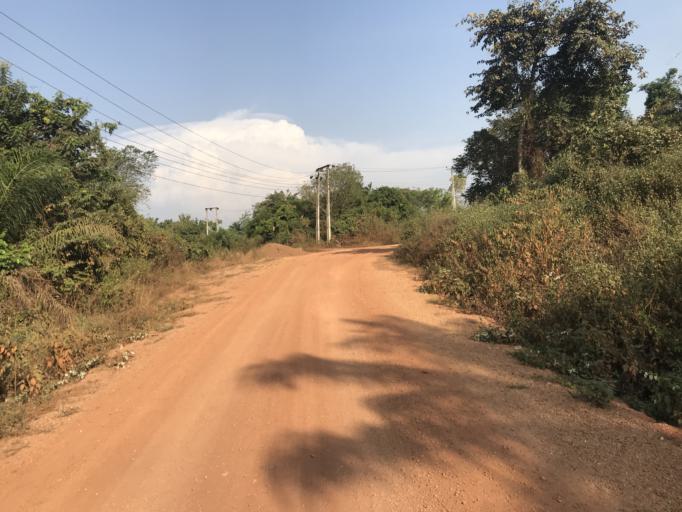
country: NG
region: Osun
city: Bode Osi
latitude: 7.7673
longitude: 4.3102
